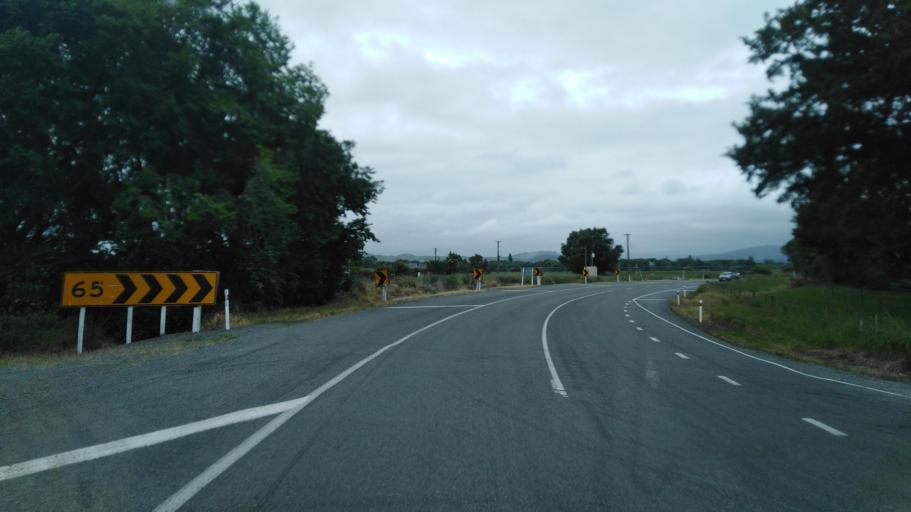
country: NZ
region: Canterbury
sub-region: Kaikoura District
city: Kaikoura
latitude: -42.7393
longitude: 173.2664
